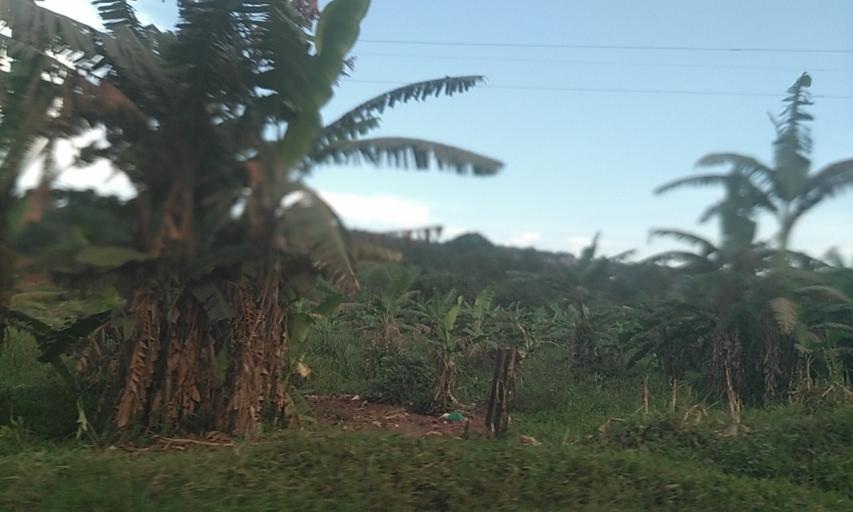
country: UG
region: Central Region
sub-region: Wakiso District
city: Kajansi
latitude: 0.2422
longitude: 32.4980
